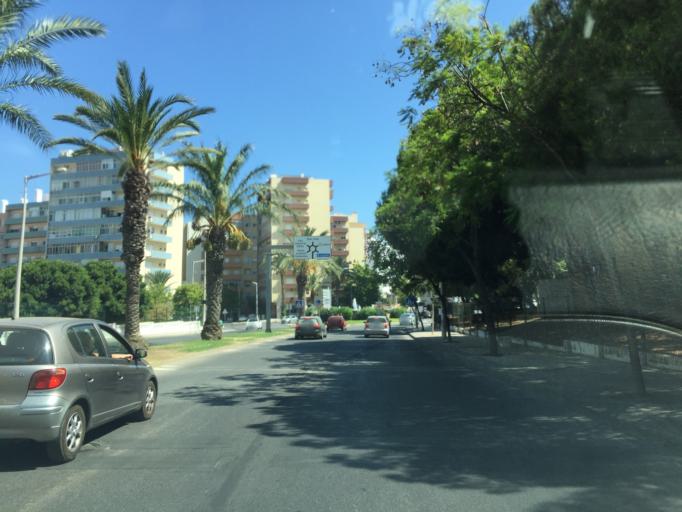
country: PT
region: Faro
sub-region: Faro
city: Faro
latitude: 37.0248
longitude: -7.9275
